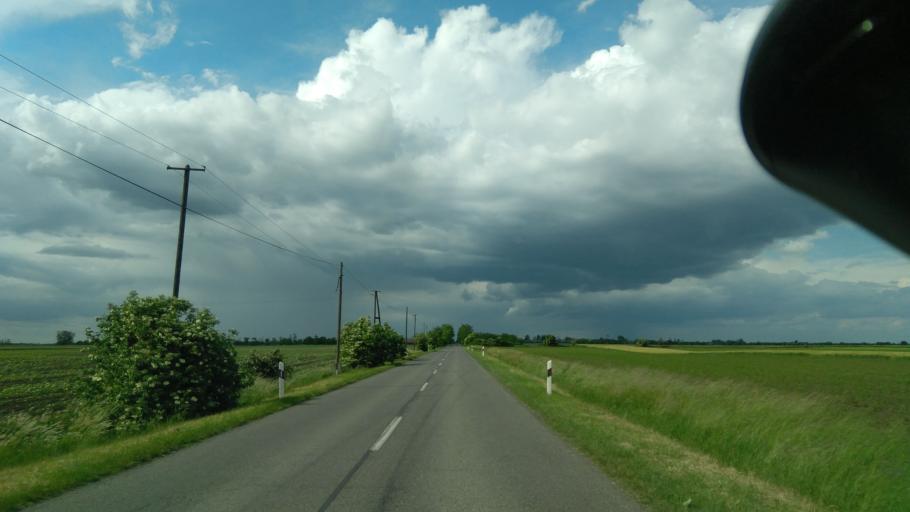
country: HU
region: Bekes
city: Gadoros
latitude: 46.6380
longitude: 20.5899
